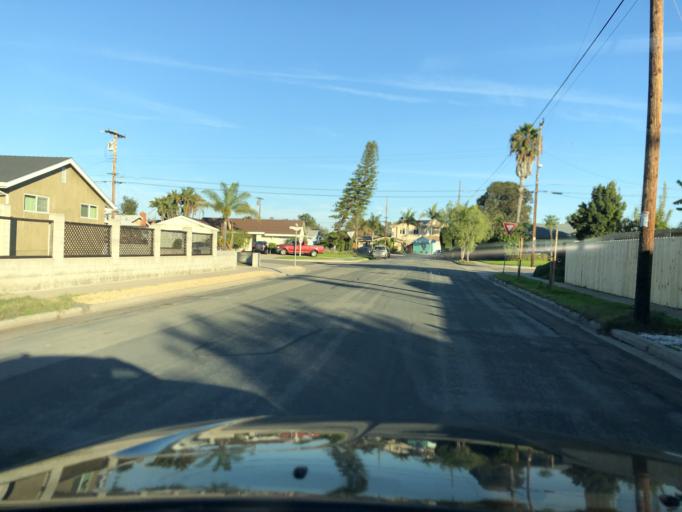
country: US
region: California
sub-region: San Diego County
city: La Jolla
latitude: 32.8186
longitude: -117.1944
